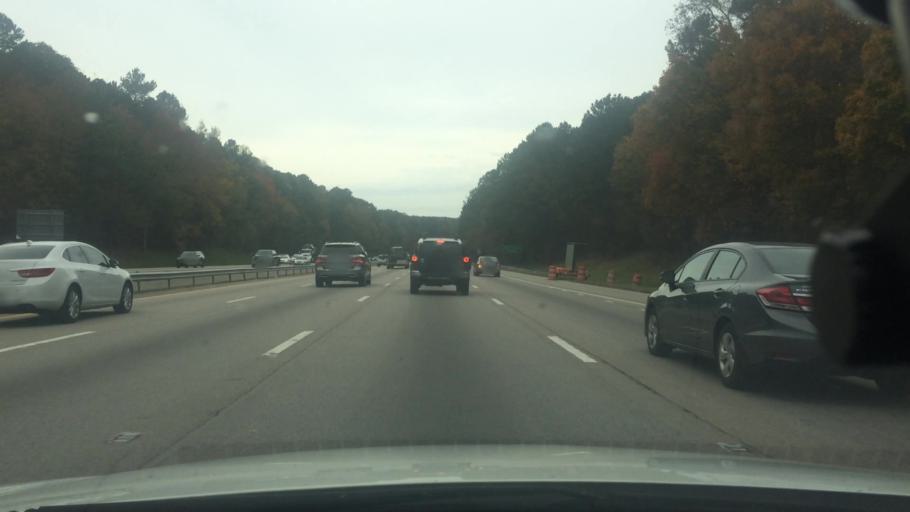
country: US
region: North Carolina
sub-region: Wake County
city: Cary
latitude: 35.8363
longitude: -78.7732
